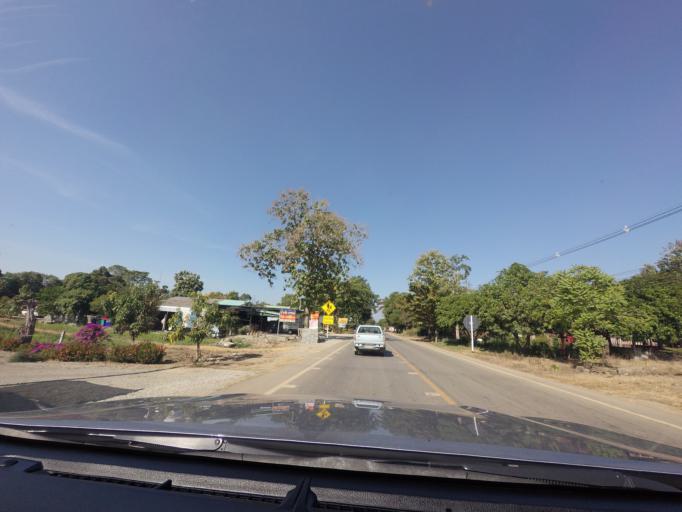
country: TH
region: Sukhothai
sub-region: Amphoe Si Satchanalai
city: Si Satchanalai
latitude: 17.6656
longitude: 99.6913
